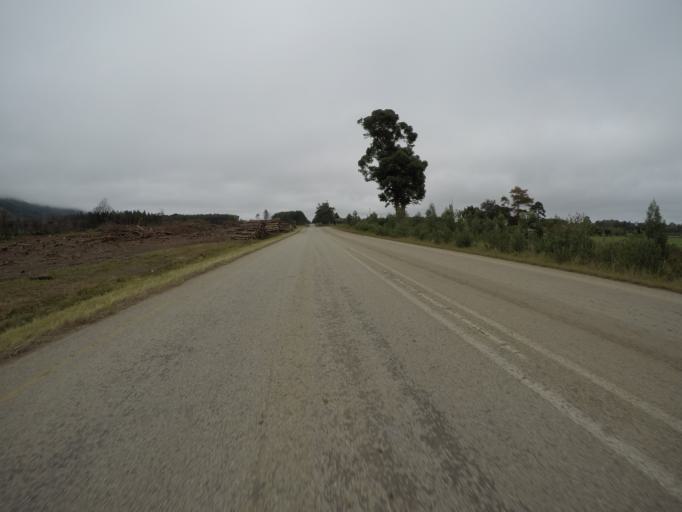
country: ZA
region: Eastern Cape
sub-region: Cacadu District Municipality
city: Kareedouw
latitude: -33.9893
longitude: 24.0796
